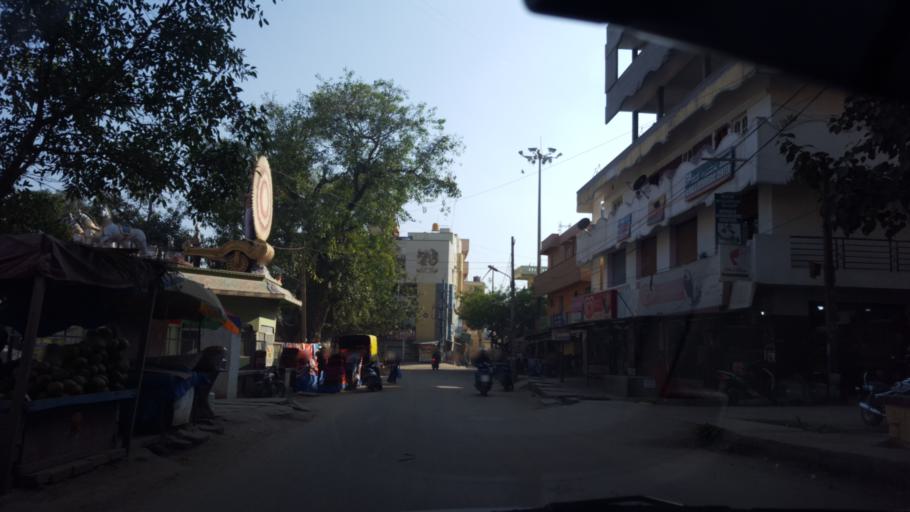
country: IN
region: Karnataka
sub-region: Bangalore Urban
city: Bangalore
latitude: 12.9488
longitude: 77.7080
